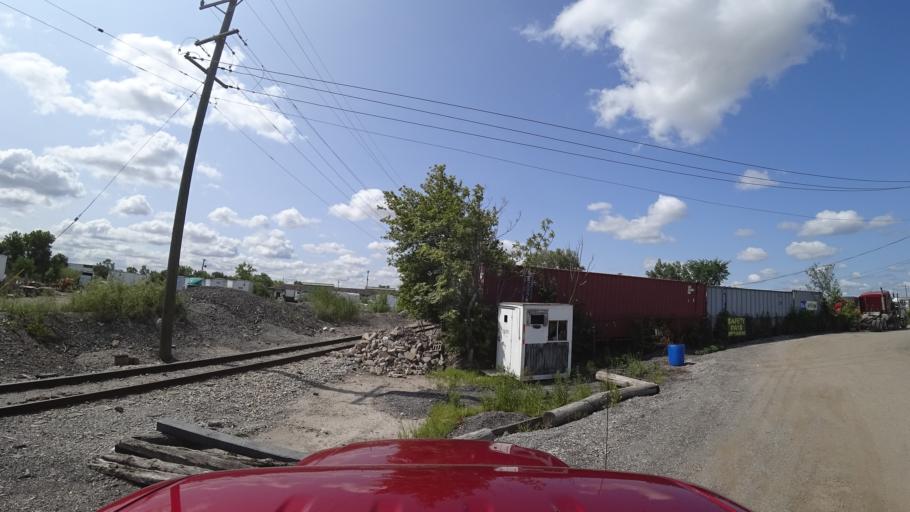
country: US
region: Illinois
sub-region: Cook County
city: Cicero
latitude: 41.8321
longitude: -87.7398
